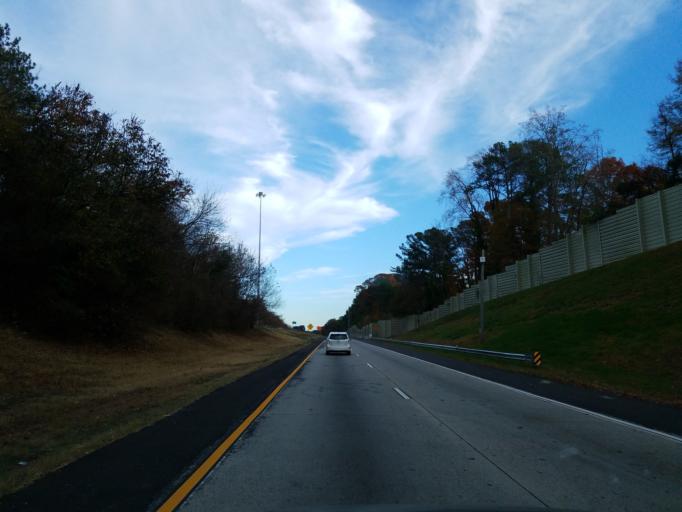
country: US
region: Georgia
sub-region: Fulton County
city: East Point
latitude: 33.7611
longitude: -84.4888
